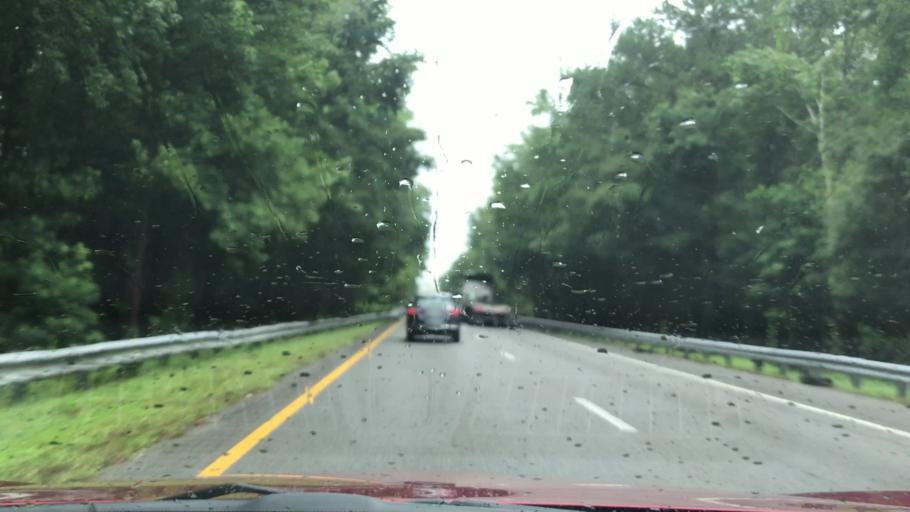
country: US
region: South Carolina
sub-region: Dorchester County
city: Ridgeville
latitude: 33.0993
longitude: -80.2409
